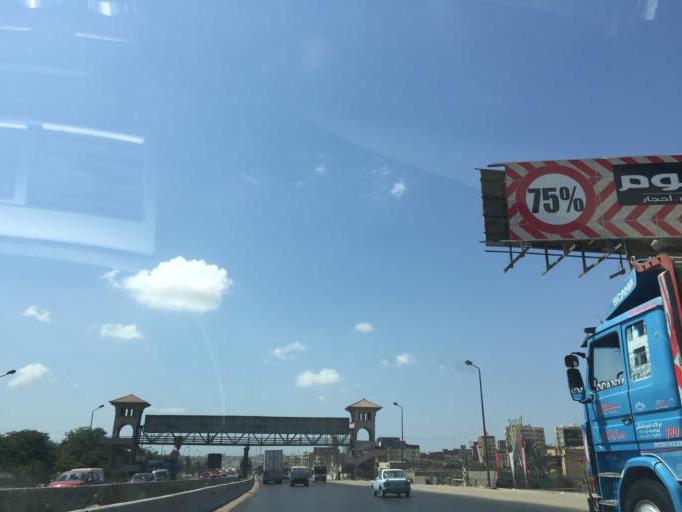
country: EG
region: Alexandria
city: Alexandria
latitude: 31.0047
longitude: 29.8051
